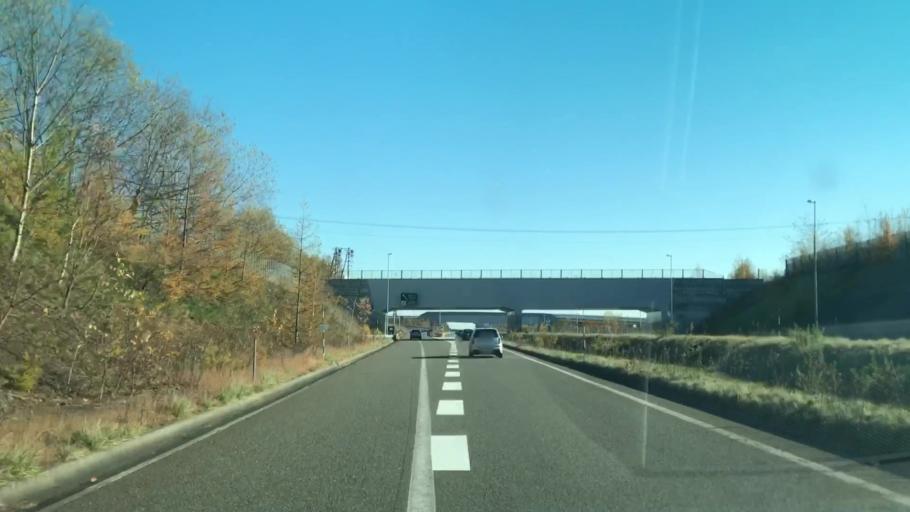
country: JP
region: Hokkaido
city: Otofuke
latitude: 42.9971
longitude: 142.8538
